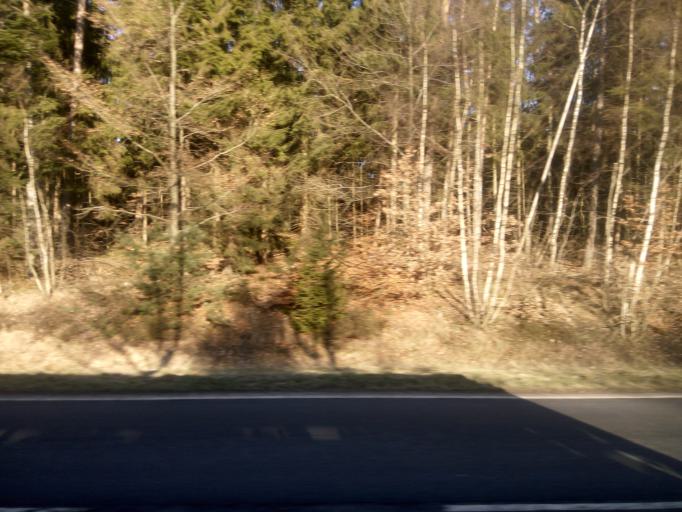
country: LU
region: Grevenmacher
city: Gonderange
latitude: 49.6739
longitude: 6.2129
